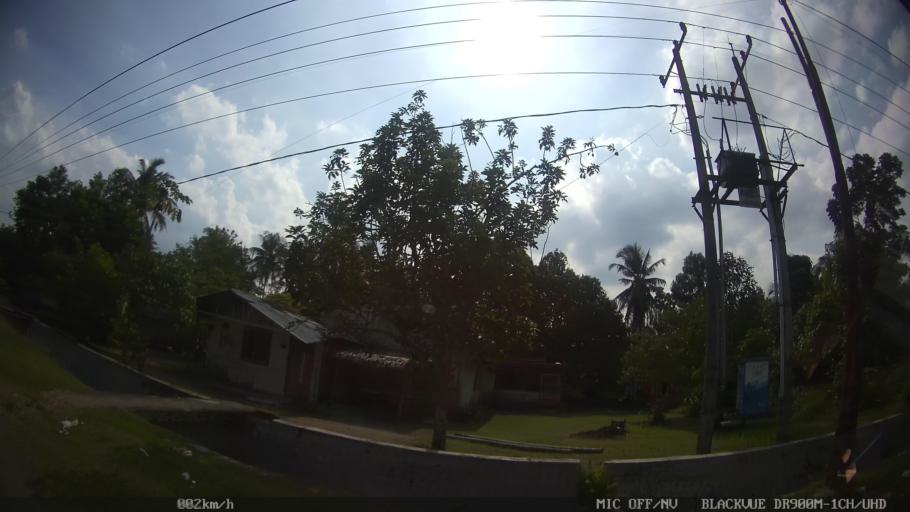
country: ID
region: North Sumatra
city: Binjai
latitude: 3.6430
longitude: 98.5178
